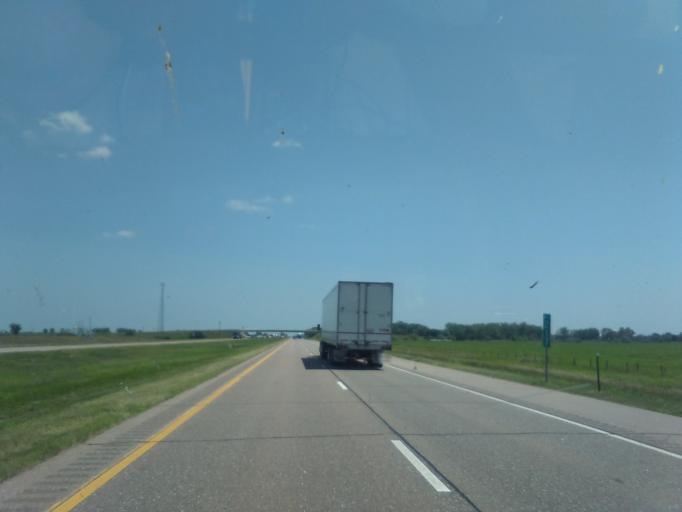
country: US
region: Nebraska
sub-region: Dawson County
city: Cozad
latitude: 40.8819
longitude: -100.0779
